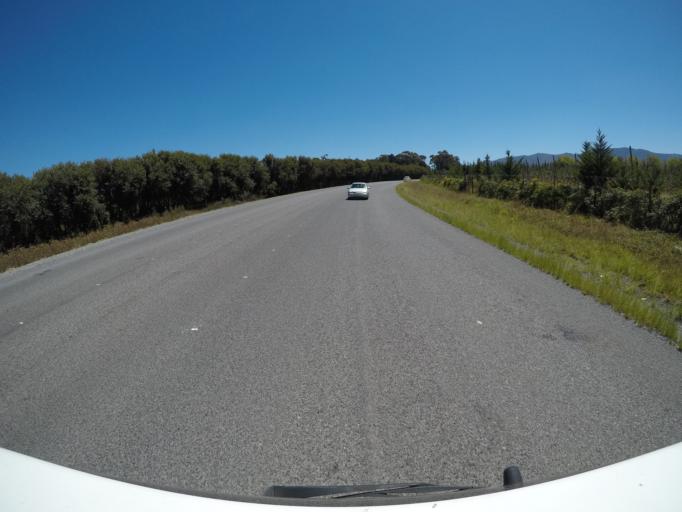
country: ZA
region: Western Cape
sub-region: Overberg District Municipality
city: Grabouw
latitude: -34.1671
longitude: 19.0363
